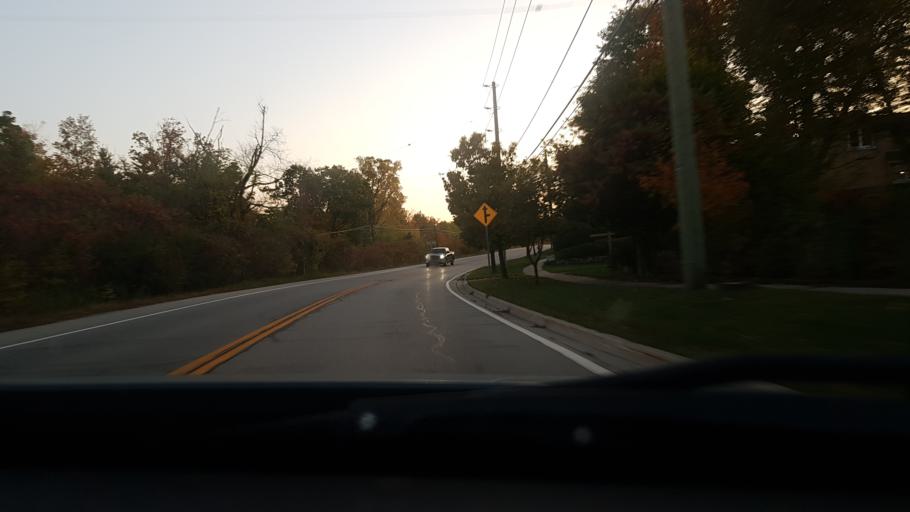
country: CA
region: Ontario
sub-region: Halton
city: Milton
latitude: 43.4847
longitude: -79.9838
